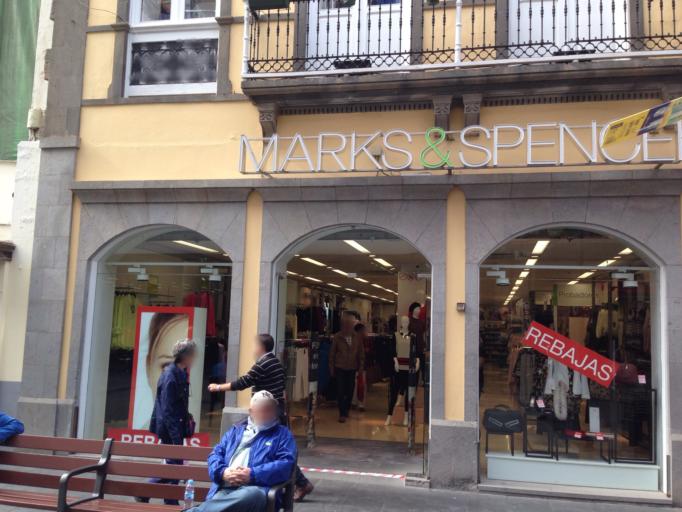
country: ES
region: Canary Islands
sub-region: Provincia de Las Palmas
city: Las Palmas de Gran Canaria
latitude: 28.1056
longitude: -15.4162
